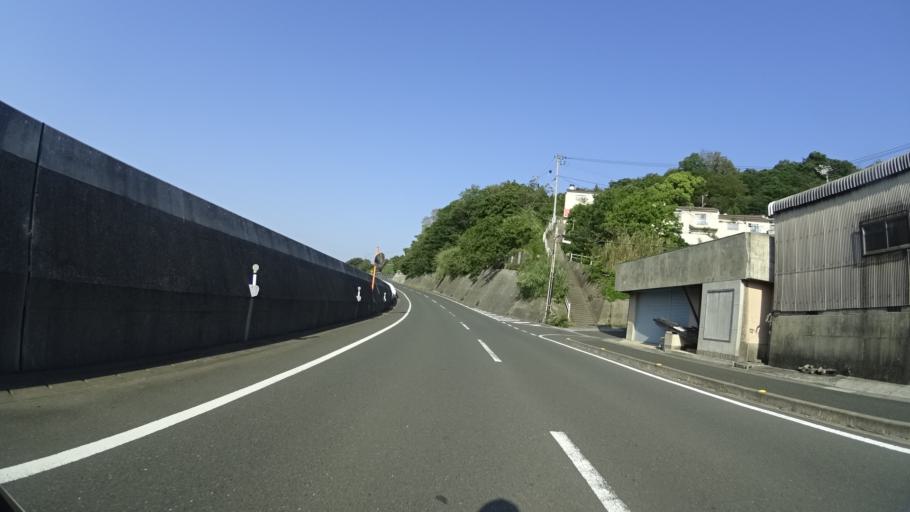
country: JP
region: Ehime
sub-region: Nishiuwa-gun
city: Ikata-cho
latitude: 33.3912
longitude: 132.1141
